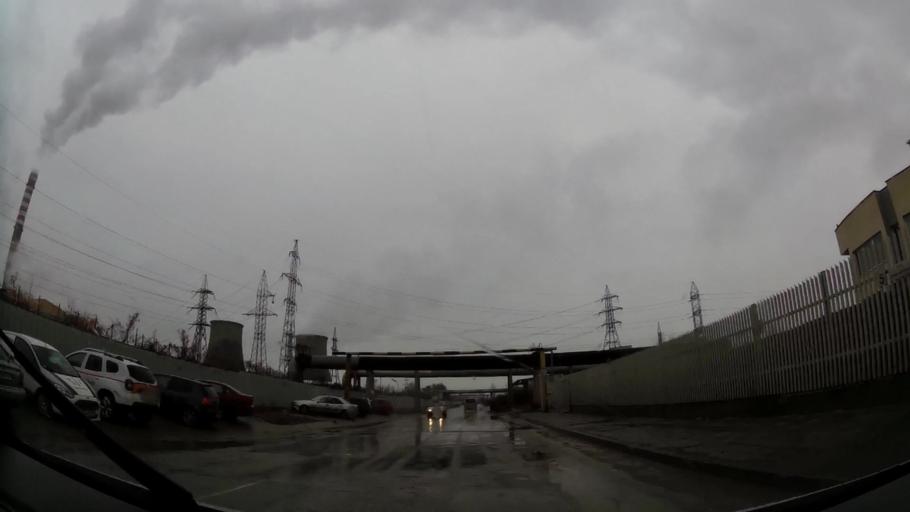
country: BG
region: Sofia-Capital
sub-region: Stolichna Obshtina
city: Sofia
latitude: 42.6530
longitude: 23.4141
